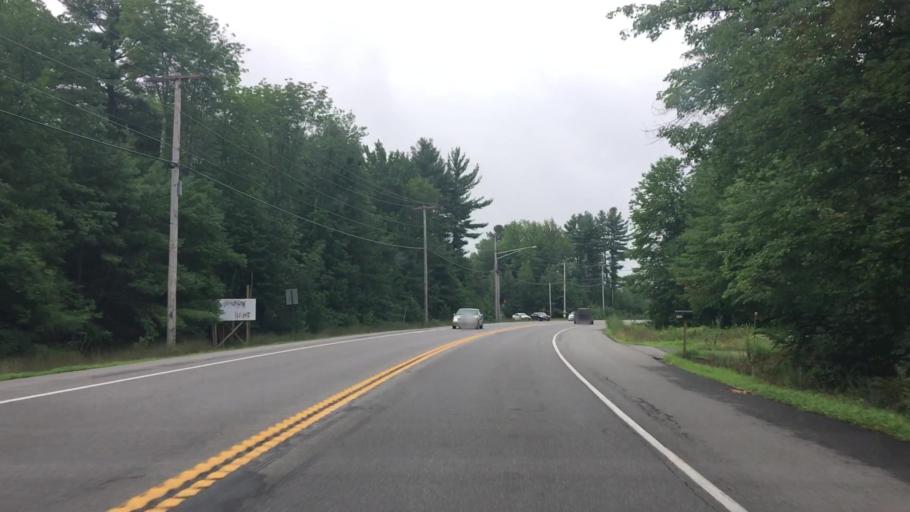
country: US
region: Maine
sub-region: York County
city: Lebanon
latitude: 43.3818
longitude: -70.8768
